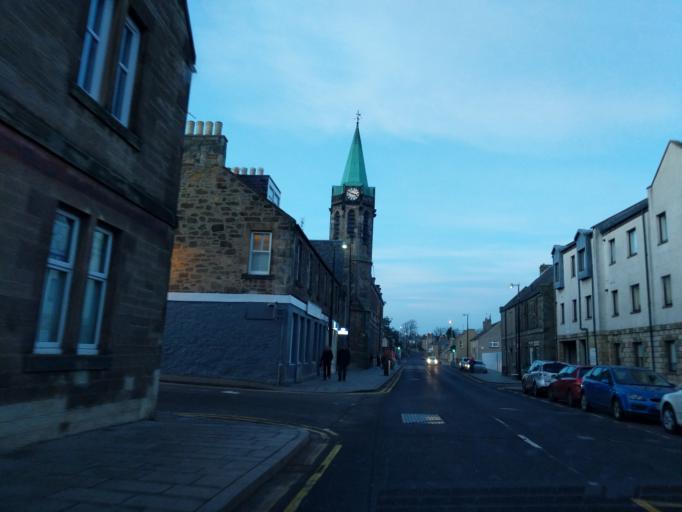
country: GB
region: Scotland
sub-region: Midlothian
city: Bonnyrigg
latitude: 55.8765
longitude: -3.1071
